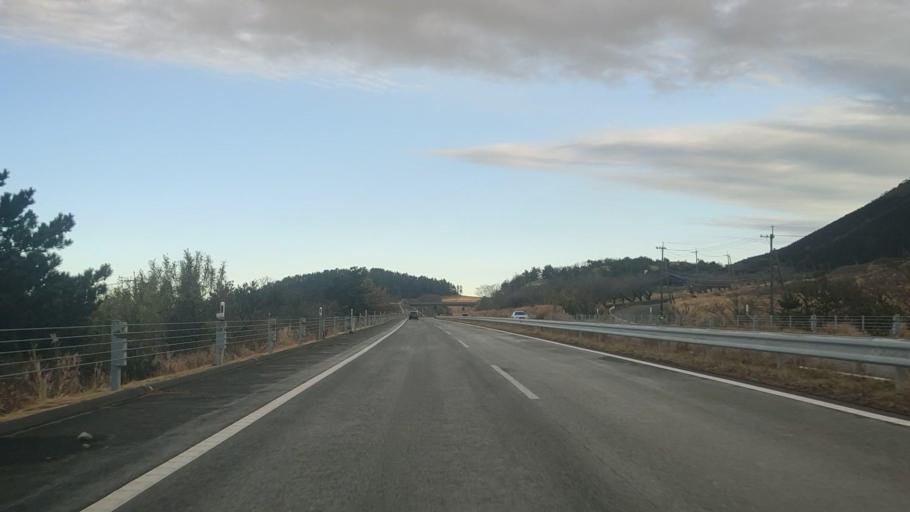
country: JP
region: Oita
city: Beppu
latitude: 33.3106
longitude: 131.4072
